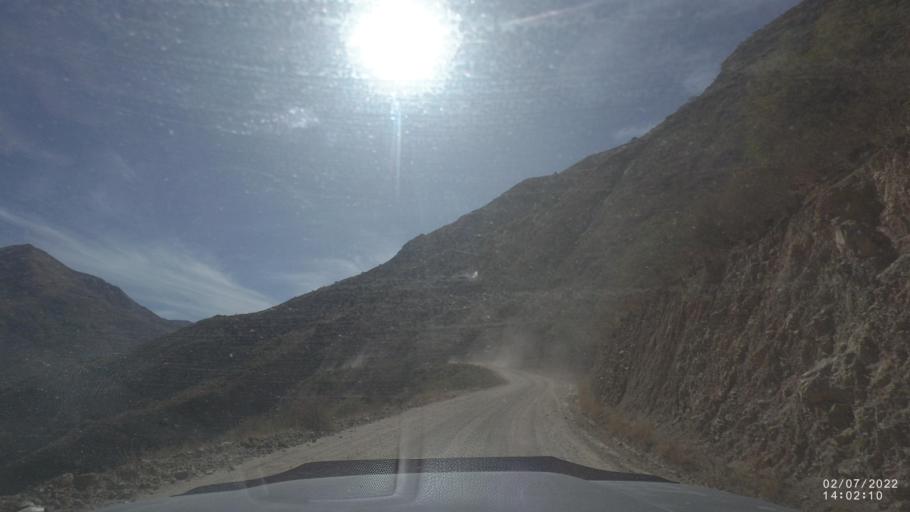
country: BO
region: Cochabamba
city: Irpa Irpa
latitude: -17.8249
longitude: -66.3864
